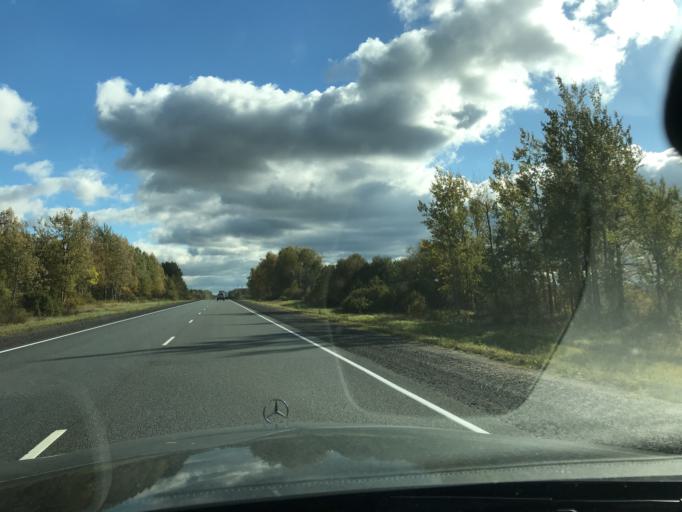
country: RU
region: Pskov
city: Ostrov
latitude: 57.0788
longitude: 28.5604
